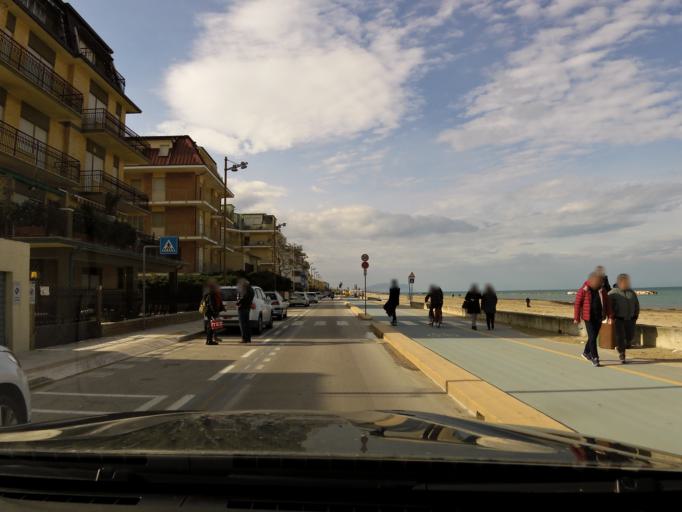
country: IT
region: The Marches
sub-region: Provincia di Macerata
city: Civitanova Marche
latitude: 43.3229
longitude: 13.7186
